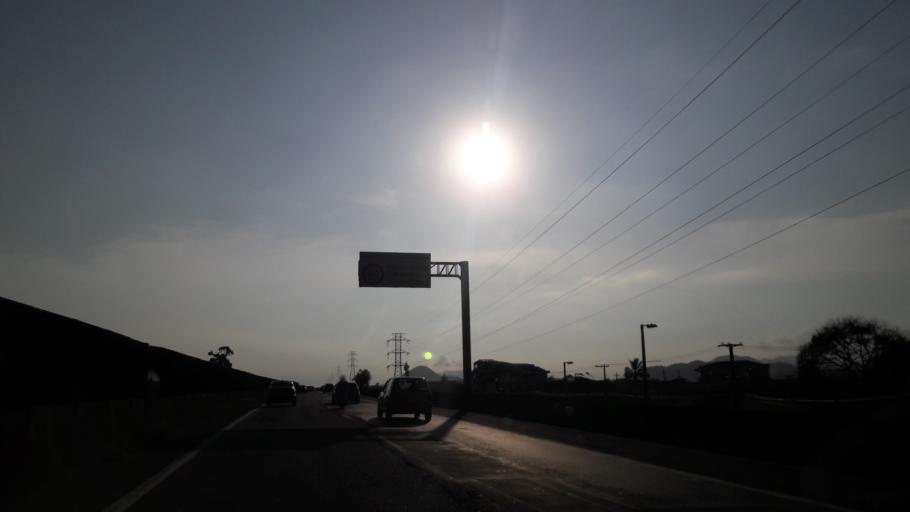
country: BR
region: Sao Paulo
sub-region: Mongagua
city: Mongagua
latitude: -24.0991
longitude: -46.6333
